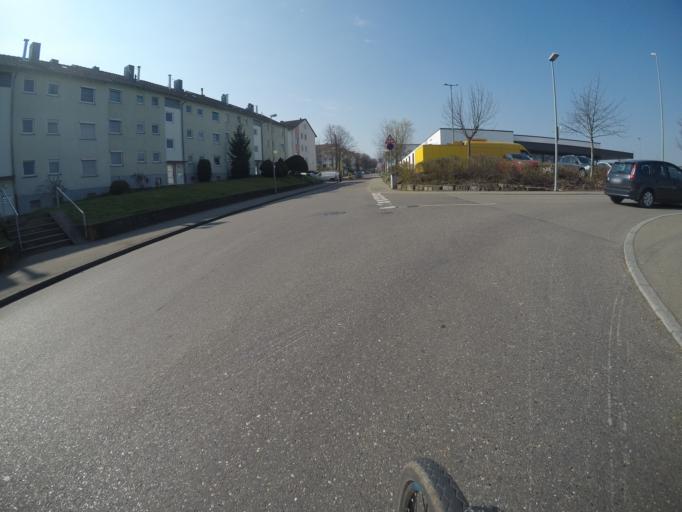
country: DE
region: Baden-Wuerttemberg
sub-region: Regierungsbezirk Stuttgart
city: Nurtingen
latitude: 48.6136
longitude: 9.3334
